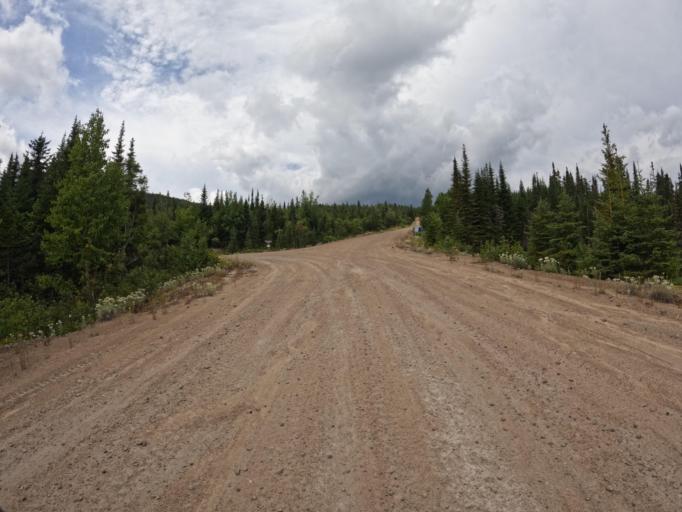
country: CA
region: Quebec
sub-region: Capitale-Nationale
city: Baie-Saint-Paul
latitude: 47.7044
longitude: -71.0114
